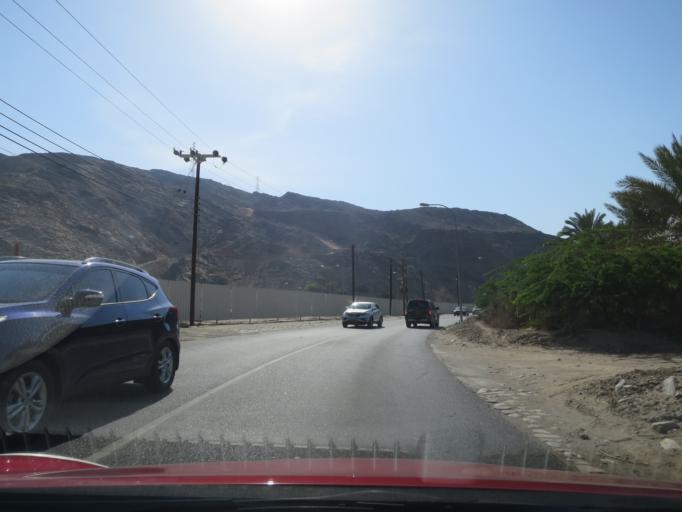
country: OM
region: Muhafazat Masqat
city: Muscat
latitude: 23.5067
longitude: 58.6542
